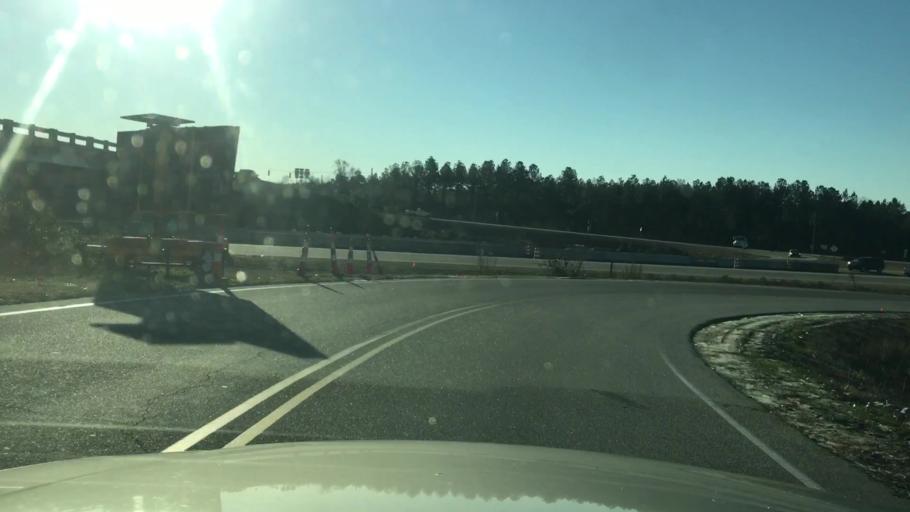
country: US
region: North Carolina
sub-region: Cumberland County
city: Hope Mills
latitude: 34.9451
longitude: -78.9317
